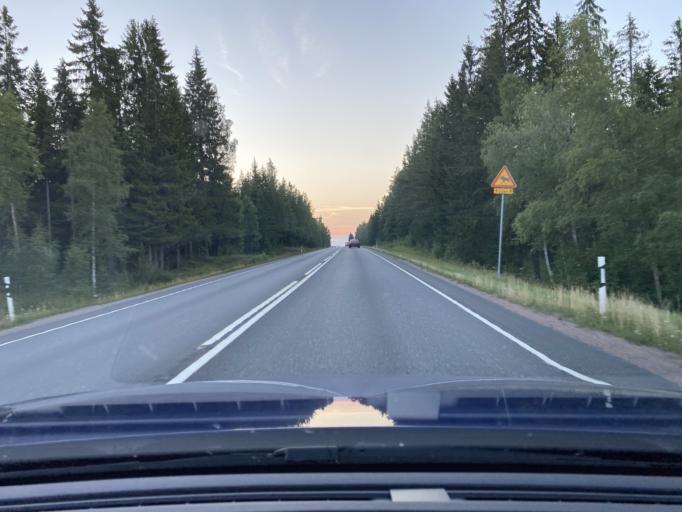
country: FI
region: Pirkanmaa
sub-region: Luoteis-Pirkanmaa
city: Ikaalinen
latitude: 61.8352
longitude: 22.9393
